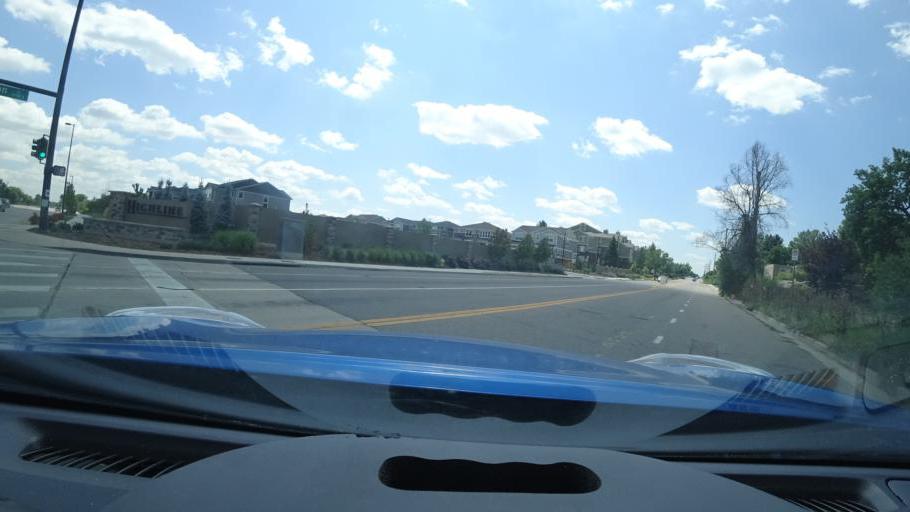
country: US
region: Colorado
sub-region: Adams County
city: Aurora
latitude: 39.6964
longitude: -104.8754
